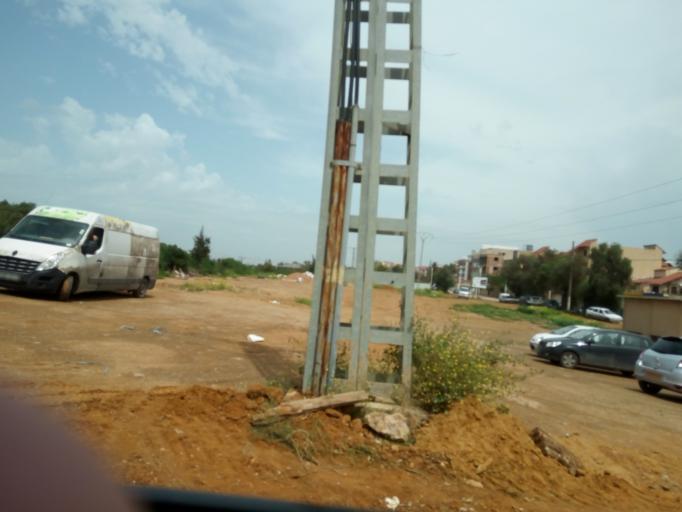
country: DZ
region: Tipaza
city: Douera
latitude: 36.6960
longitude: 2.9639
